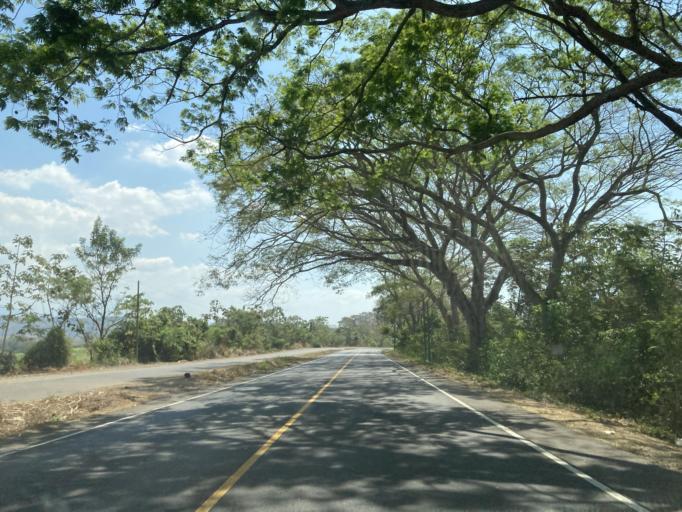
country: GT
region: Escuintla
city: Guanagazapa
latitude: 14.1756
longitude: -90.6816
